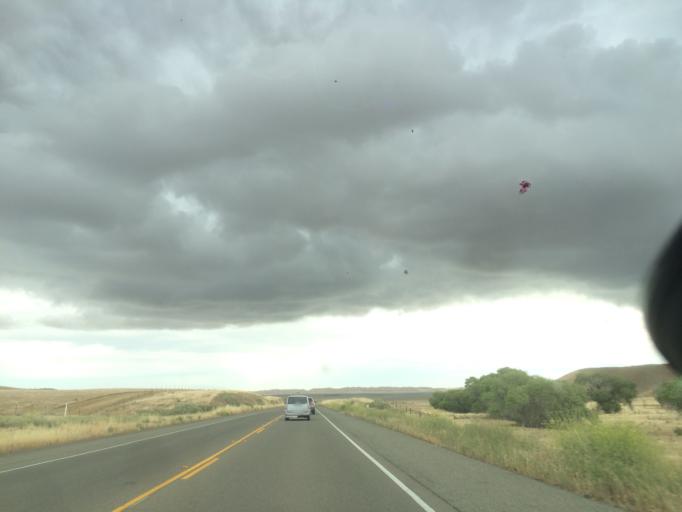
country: US
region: California
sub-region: Kings County
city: Avenal
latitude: 35.7780
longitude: -120.1343
